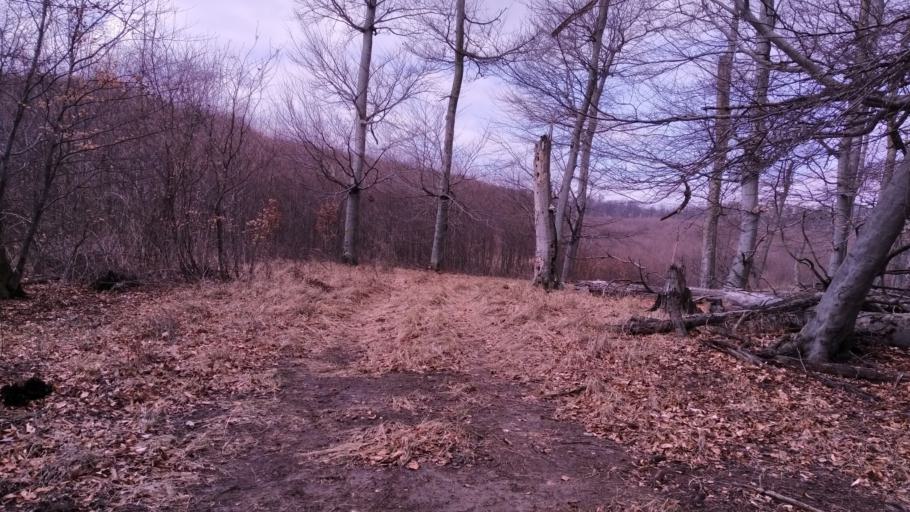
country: HU
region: Komarom-Esztergom
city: Oroszlany
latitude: 47.4045
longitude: 18.3315
